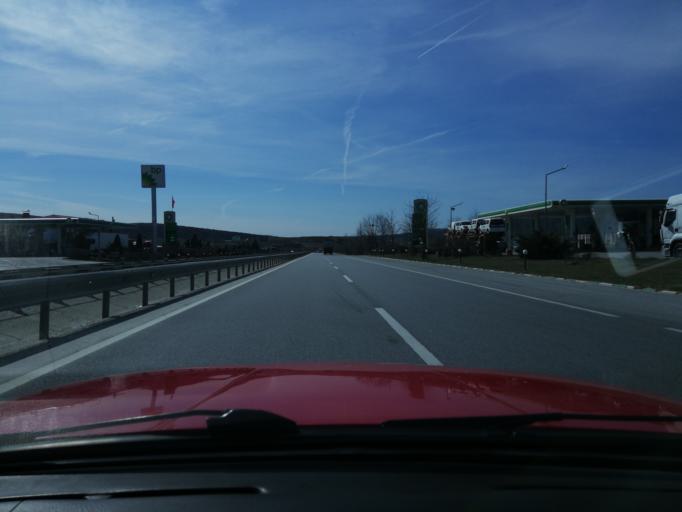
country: TR
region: Eskisehir
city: Inonu
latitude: 39.6918
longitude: 30.1555
